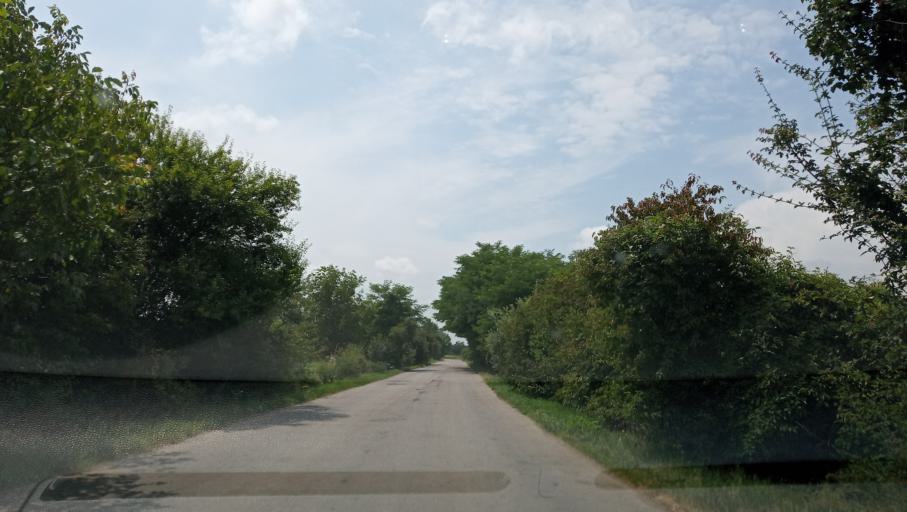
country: RO
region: Gorj
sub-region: Comuna Turcinesti
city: Turcinesti
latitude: 45.1211
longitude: 23.3299
